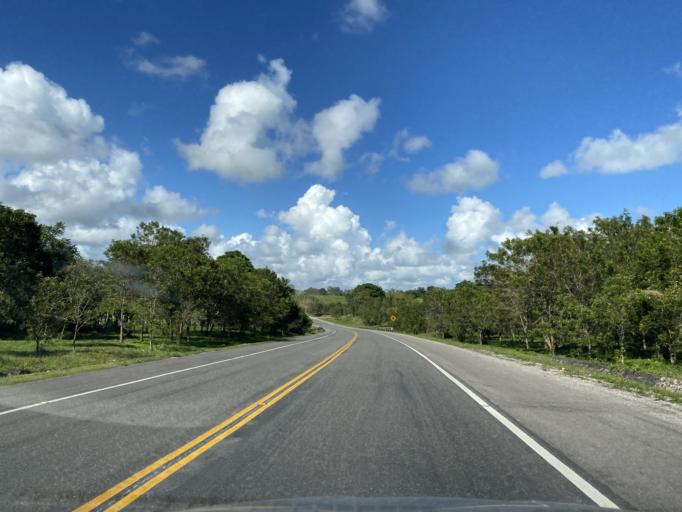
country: DO
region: Monte Plata
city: Majagual
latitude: 19.0226
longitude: -69.8226
